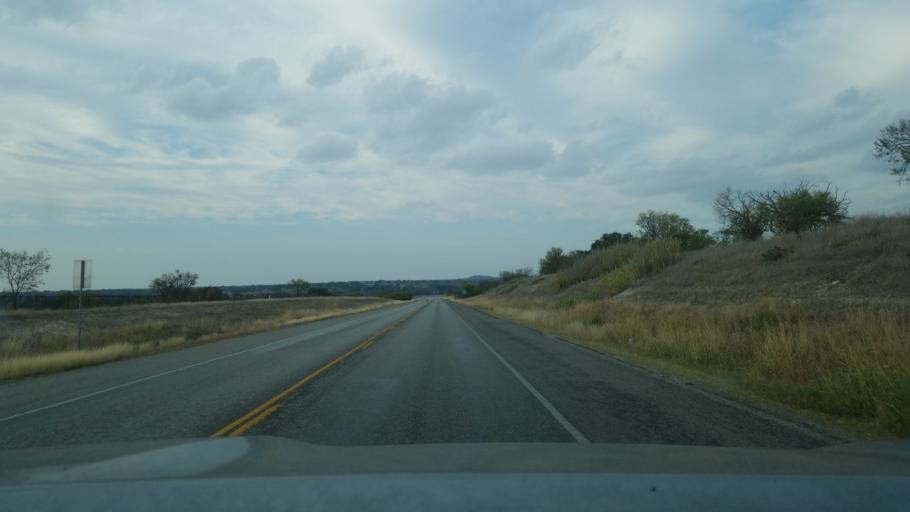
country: US
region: Texas
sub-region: Mills County
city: Goldthwaite
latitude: 31.5040
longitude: -98.5802
